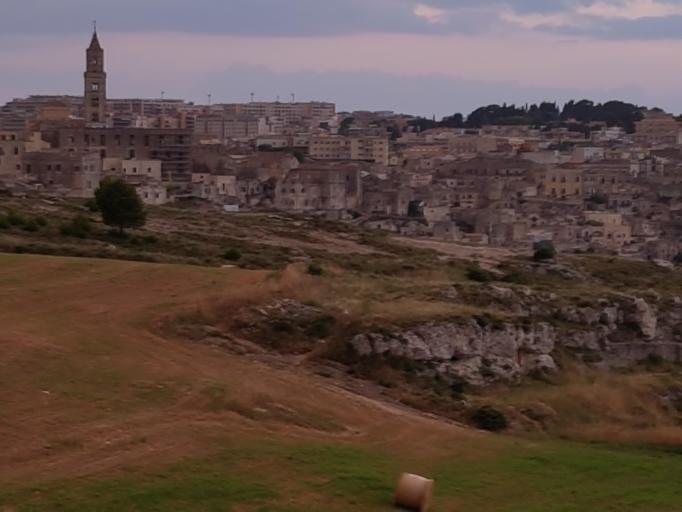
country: IT
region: Basilicate
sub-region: Provincia di Matera
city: Matera
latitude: 40.6667
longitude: 16.6214
